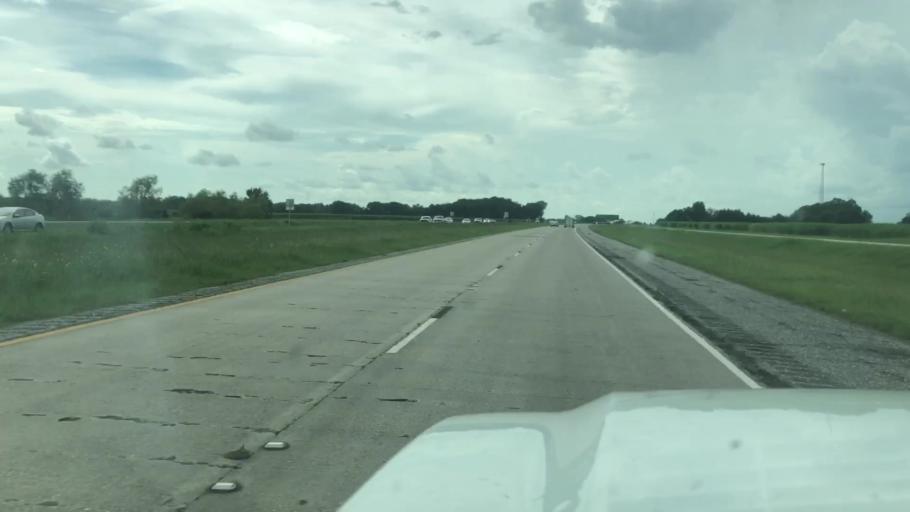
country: US
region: Louisiana
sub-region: Iberia Parish
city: Jeanerette
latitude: 29.8599
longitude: -91.6190
